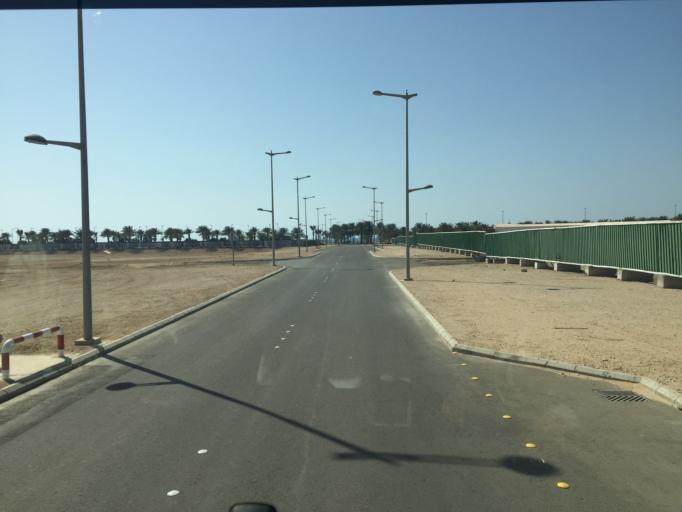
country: SA
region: Makkah
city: Rabigh
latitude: 22.4113
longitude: 39.0809
